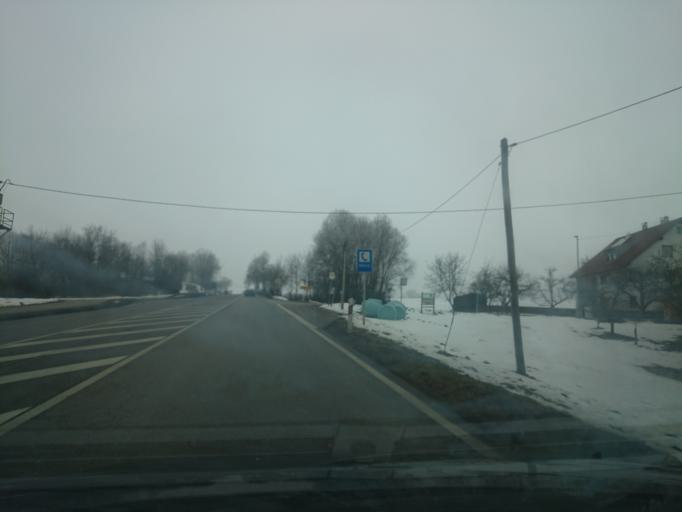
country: DE
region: Bavaria
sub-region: Swabia
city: Friedberg
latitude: 48.3756
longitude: 11.0071
